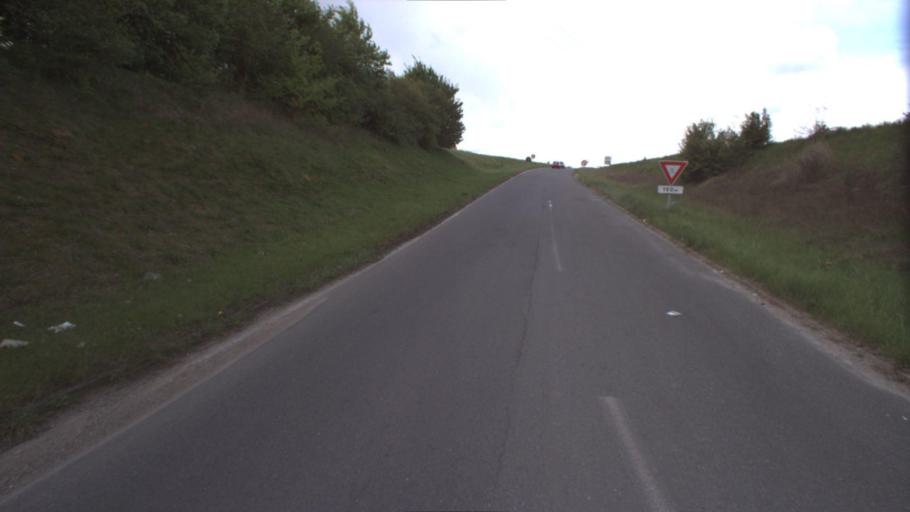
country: FR
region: Ile-de-France
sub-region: Departement de Seine-et-Marne
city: Rozay-en-Brie
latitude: 48.6852
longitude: 2.9370
